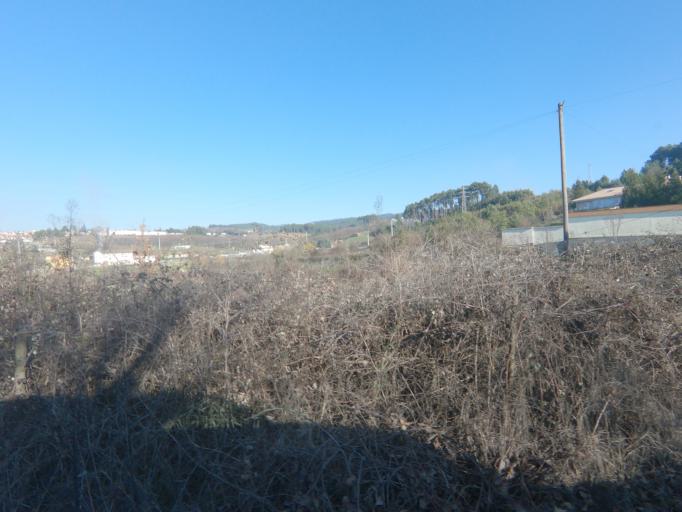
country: PT
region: Vila Real
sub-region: Vila Real
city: Vila Real
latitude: 41.2881
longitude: -7.7257
